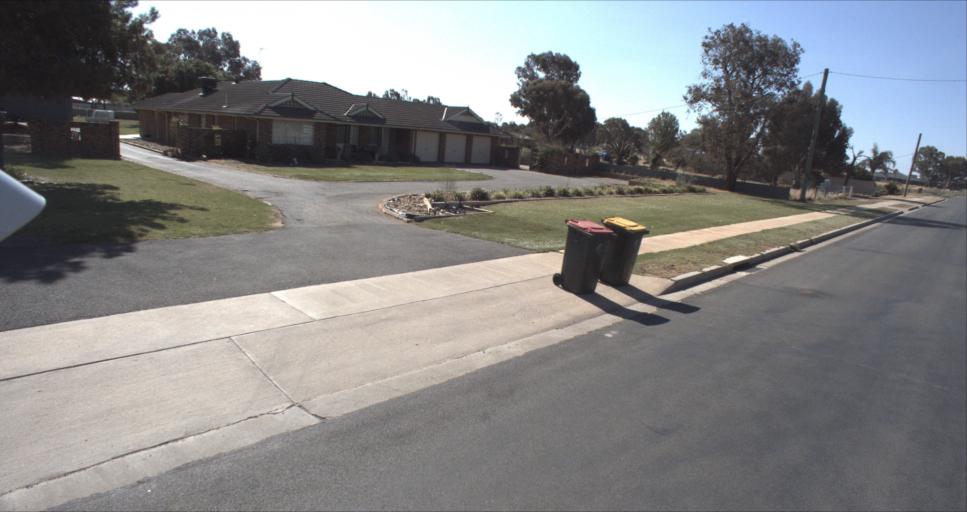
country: AU
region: New South Wales
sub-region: Leeton
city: Leeton
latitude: -34.5475
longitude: 146.4178
